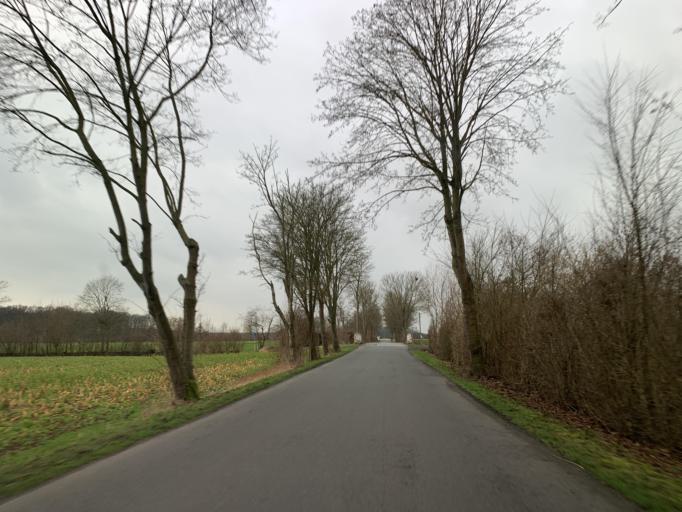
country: DE
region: North Rhine-Westphalia
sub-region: Regierungsbezirk Munster
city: Senden
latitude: 51.8793
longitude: 7.4628
